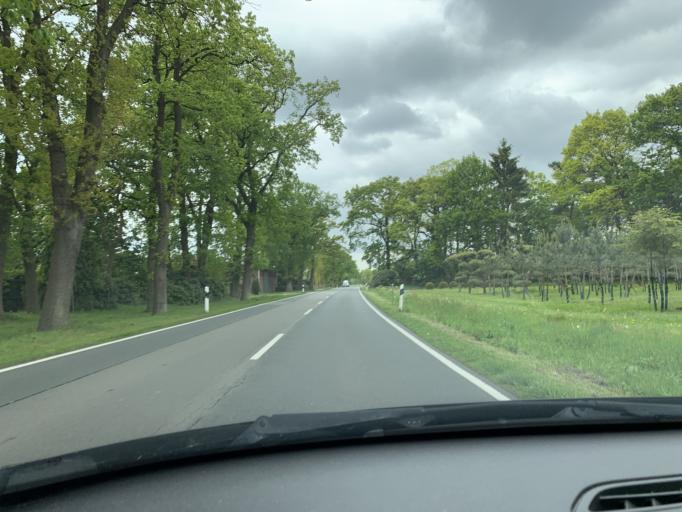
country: DE
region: Lower Saxony
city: Bad Zwischenahn
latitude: 53.1845
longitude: 8.0634
